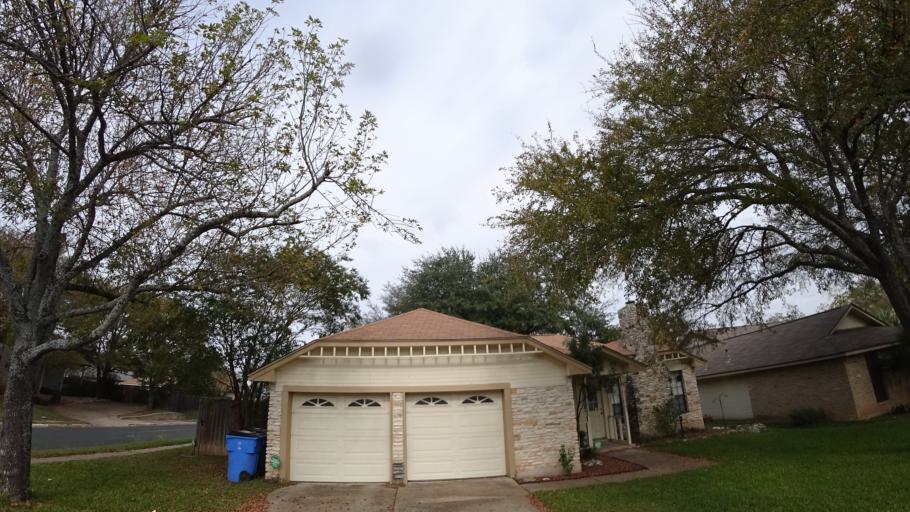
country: US
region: Texas
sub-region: Travis County
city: Wells Branch
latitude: 30.4456
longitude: -97.6847
